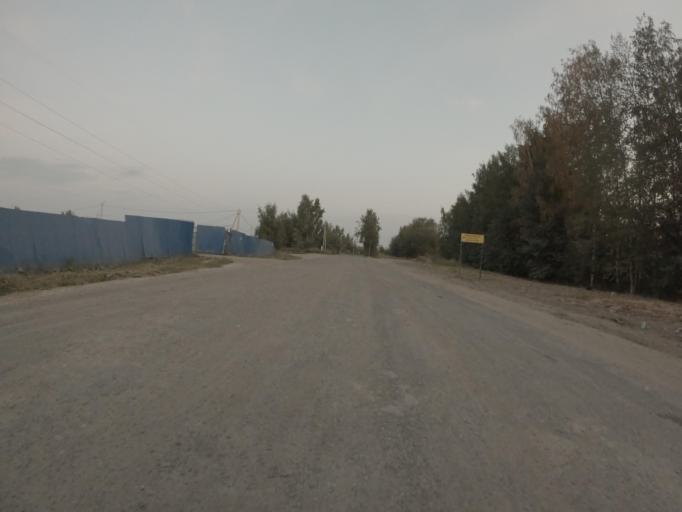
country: RU
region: Leningrad
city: Yanino Vtoroye
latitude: 59.9379
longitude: 30.5998
